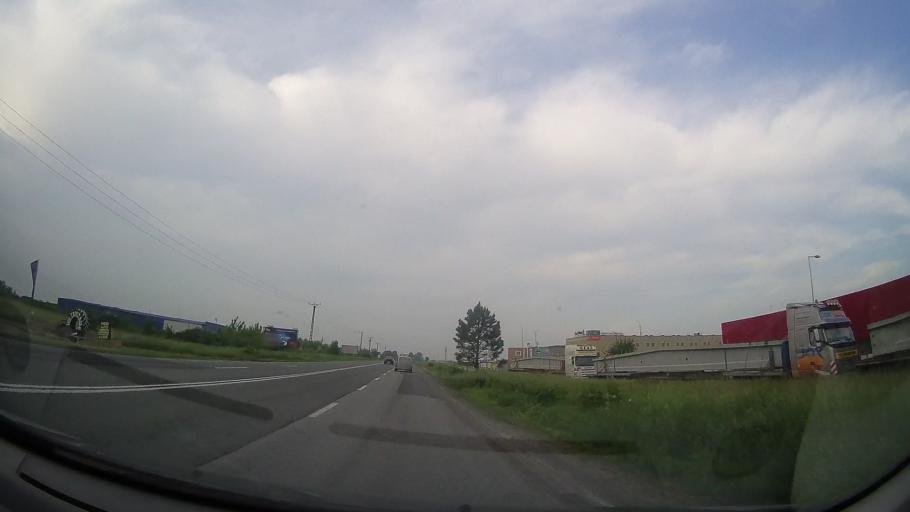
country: RO
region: Timis
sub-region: Comuna Giroc
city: Chisoda
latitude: 45.6966
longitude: 21.1788
